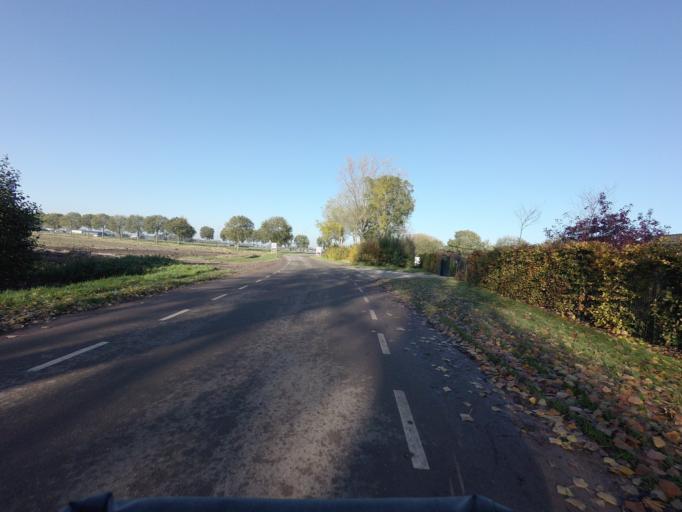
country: NL
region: North Brabant
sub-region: Gemeente Woudrichem
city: Woudrichem
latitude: 51.7722
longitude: 5.0492
